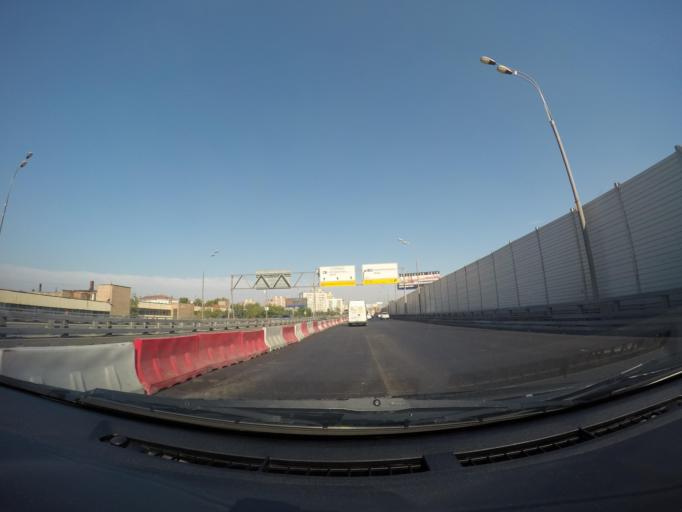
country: RU
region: Moscow
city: Lefortovo
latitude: 55.7316
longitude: 37.7044
